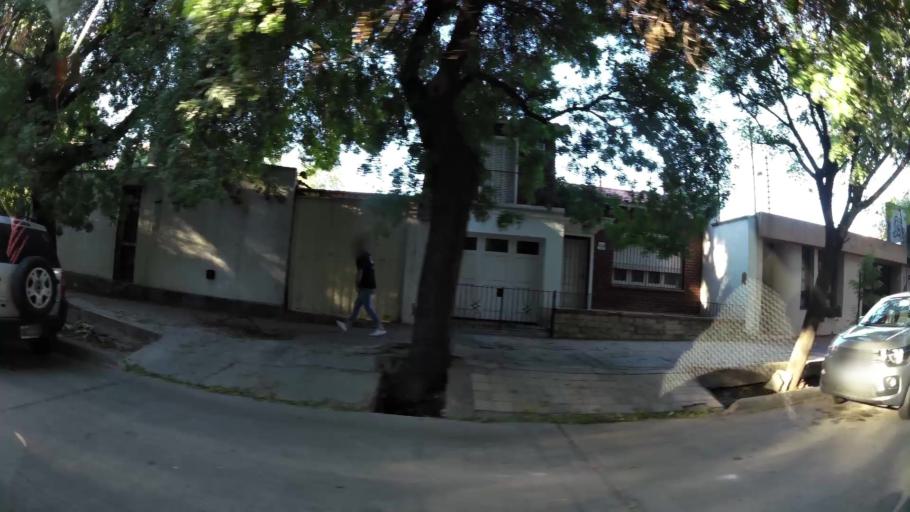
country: AR
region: Mendoza
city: Mendoza
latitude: -32.8793
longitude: -68.8447
